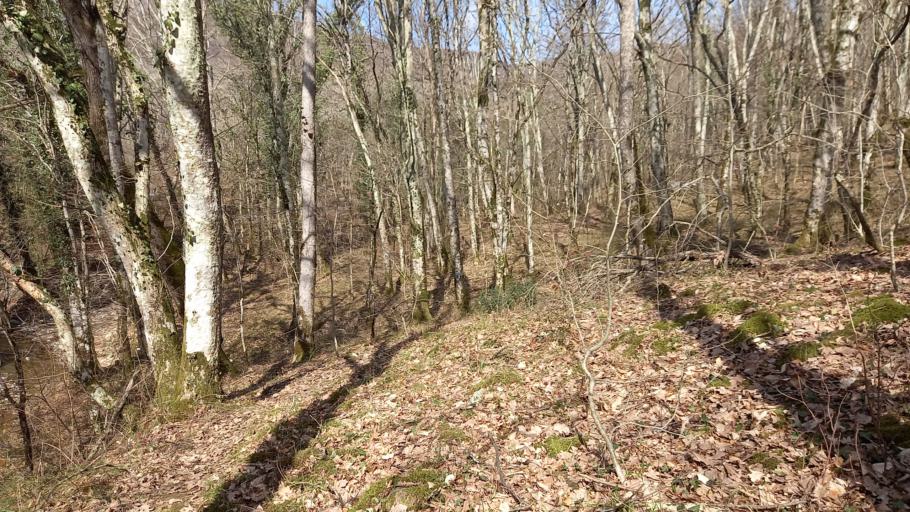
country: RU
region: Krasnodarskiy
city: Arkhipo-Osipovka
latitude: 44.3824
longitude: 38.6017
